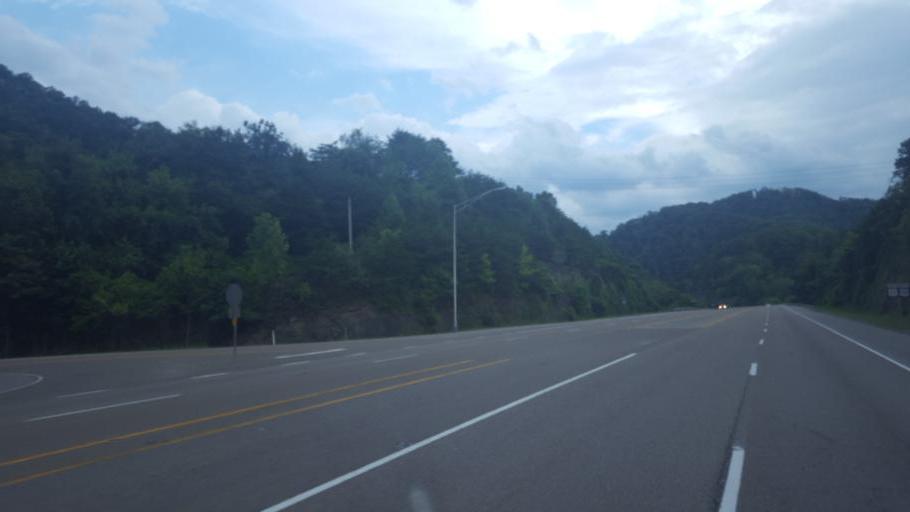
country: US
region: Kentucky
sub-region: Pike County
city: Pikeville
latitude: 37.3895
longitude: -82.5364
